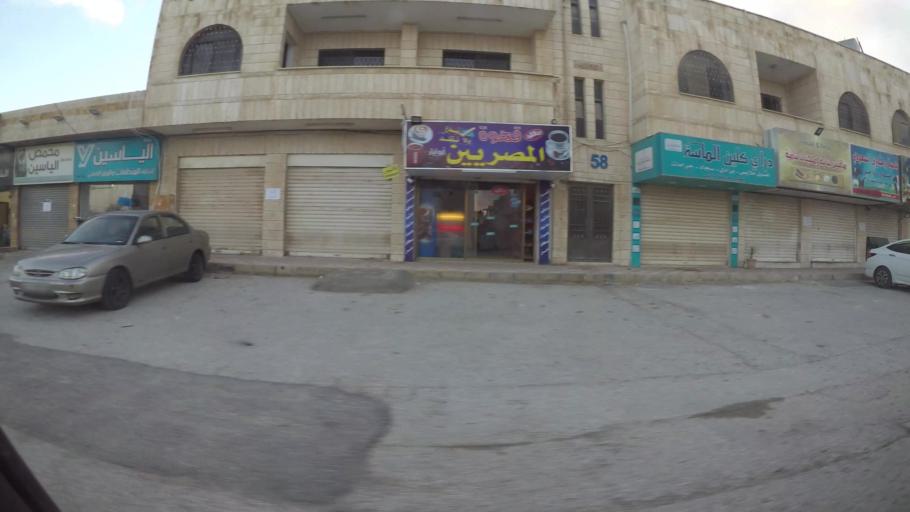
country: JO
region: Amman
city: Al Jubayhah
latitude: 32.0511
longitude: 35.9018
